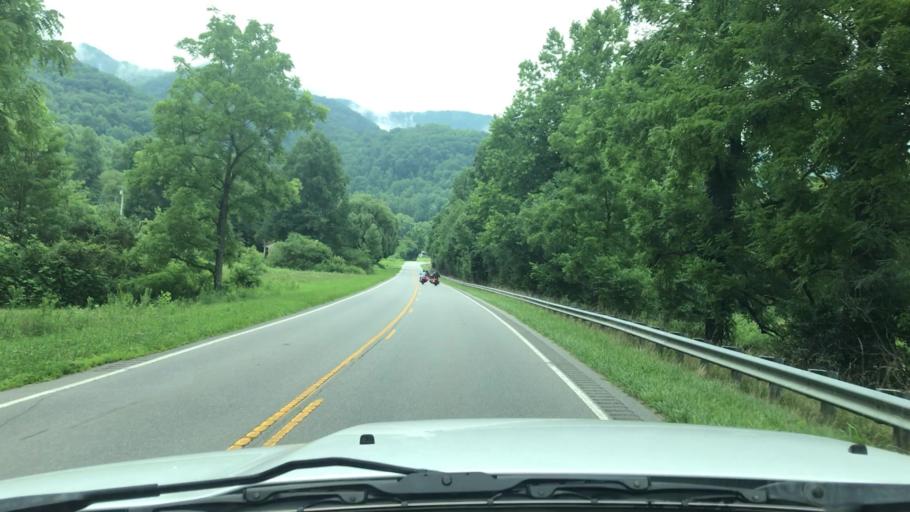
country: US
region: North Carolina
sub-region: Graham County
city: Robbinsville
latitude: 35.2730
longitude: -83.7462
